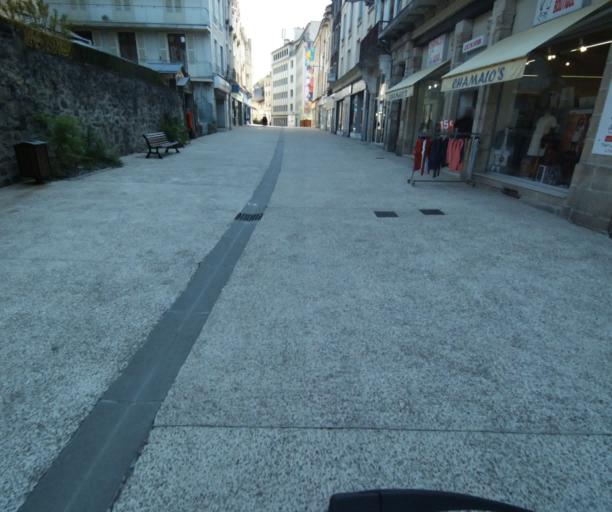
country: FR
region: Limousin
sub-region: Departement de la Correze
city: Tulle
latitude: 45.2645
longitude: 1.7684
